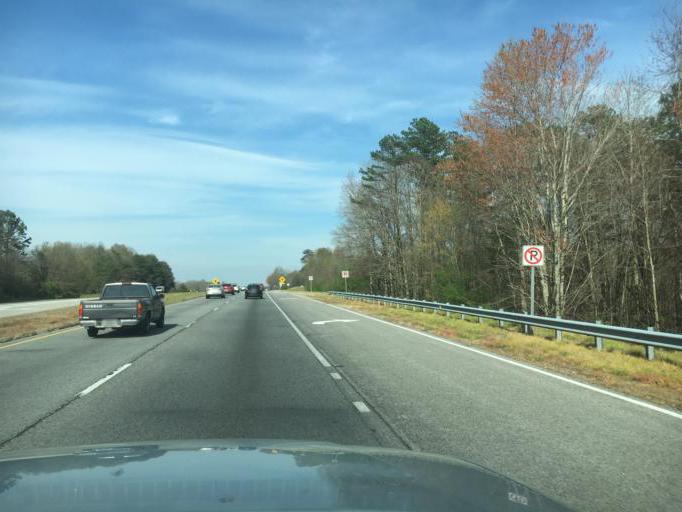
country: US
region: Georgia
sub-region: Hall County
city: Lula
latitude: 34.4073
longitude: -83.6713
